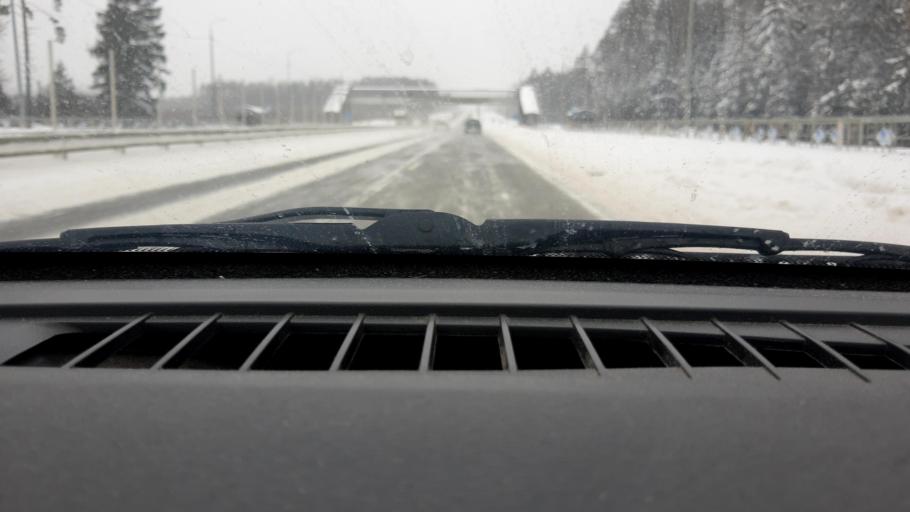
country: RU
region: Vladimir
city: Pokrov
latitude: 55.9278
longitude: 39.3155
